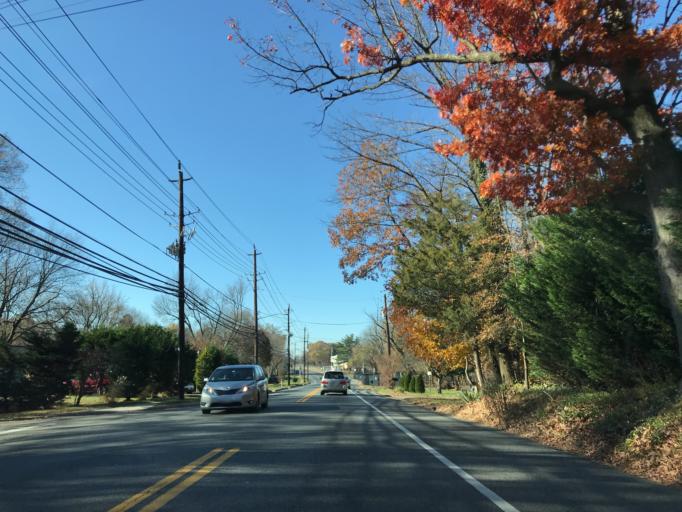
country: US
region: Maryland
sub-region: Montgomery County
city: Hillandale
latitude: 39.0289
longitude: -76.9598
